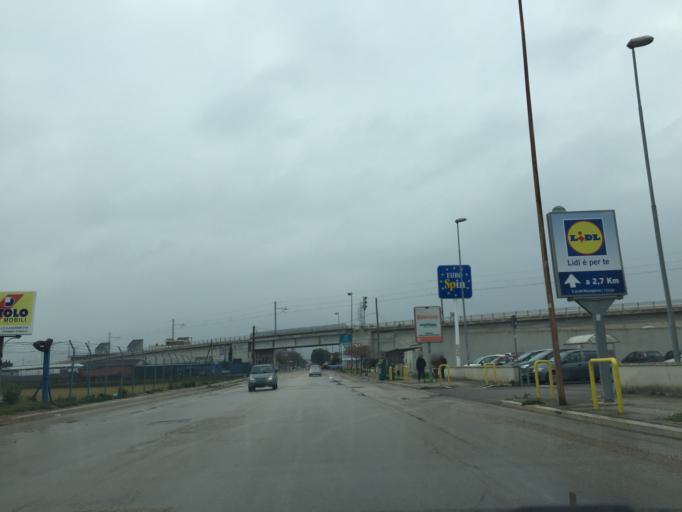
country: IT
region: Apulia
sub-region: Provincia di Foggia
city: Foggia
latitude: 41.4739
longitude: 15.5362
